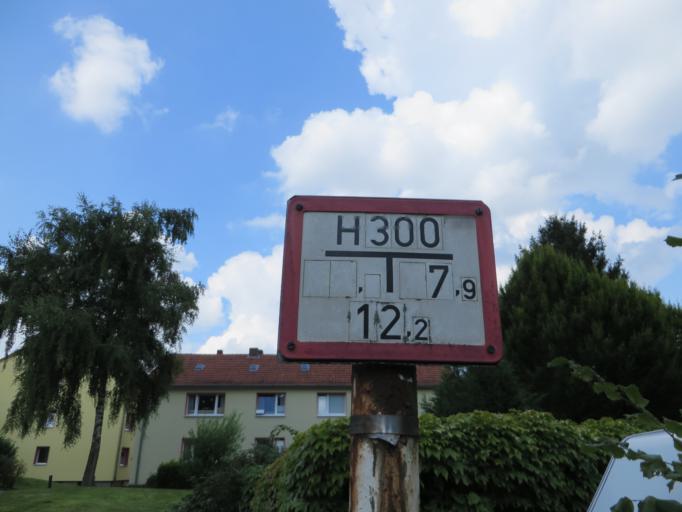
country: DE
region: North Rhine-Westphalia
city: Witten
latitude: 51.4489
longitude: 7.3936
